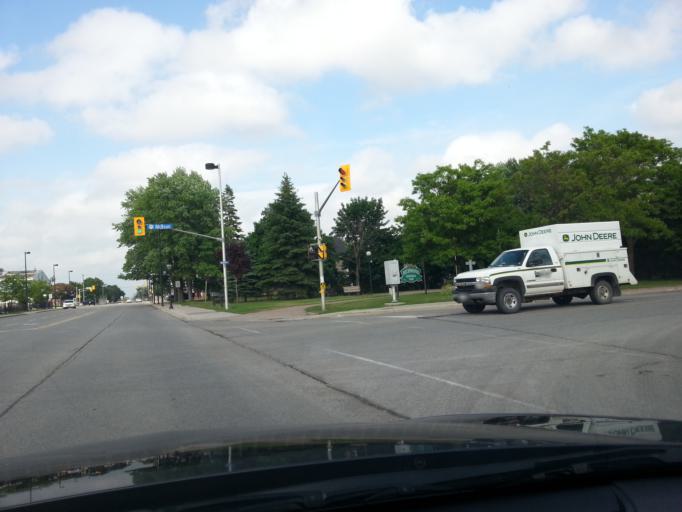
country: CA
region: Ontario
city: Bells Corners
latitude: 45.1942
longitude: -75.8390
